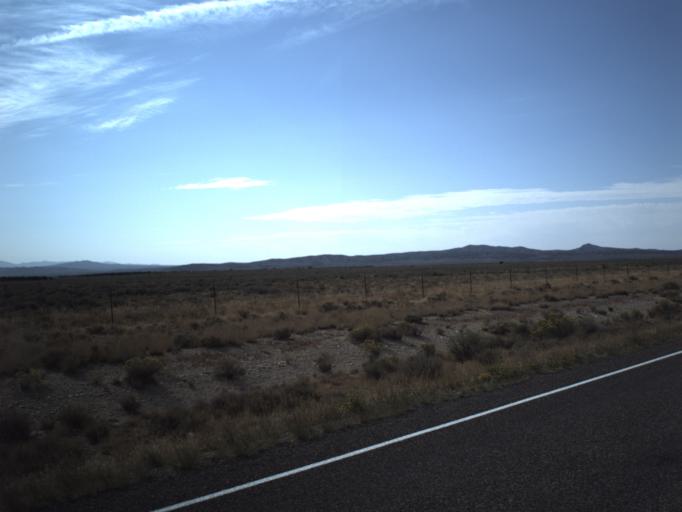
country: US
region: Idaho
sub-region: Cassia County
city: Burley
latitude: 41.7560
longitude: -113.5140
